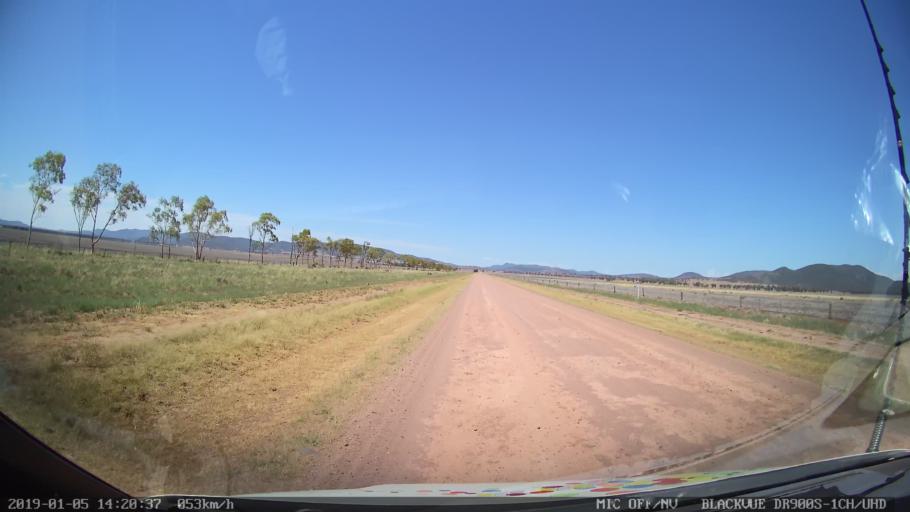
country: AU
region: New South Wales
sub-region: Liverpool Plains
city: Quirindi
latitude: -31.2482
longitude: 150.5064
